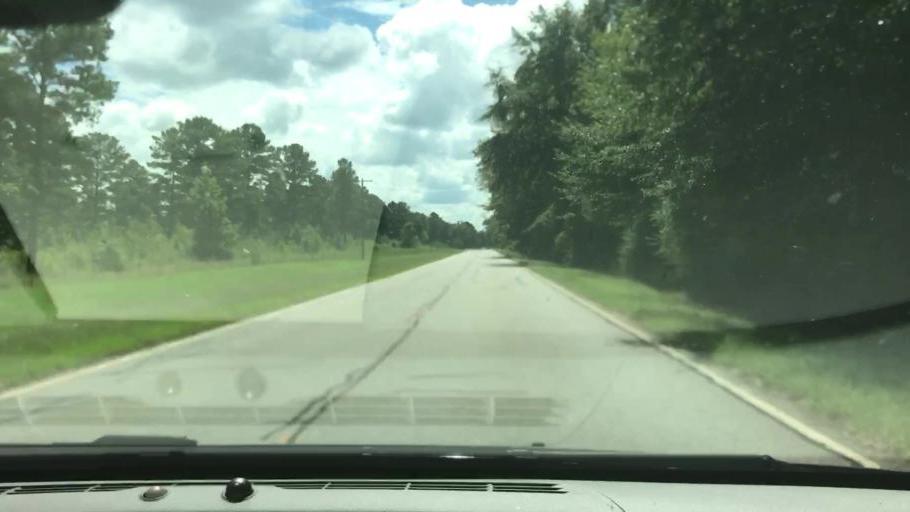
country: US
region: Georgia
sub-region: Quitman County
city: Georgetown
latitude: 32.1085
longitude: -85.0382
